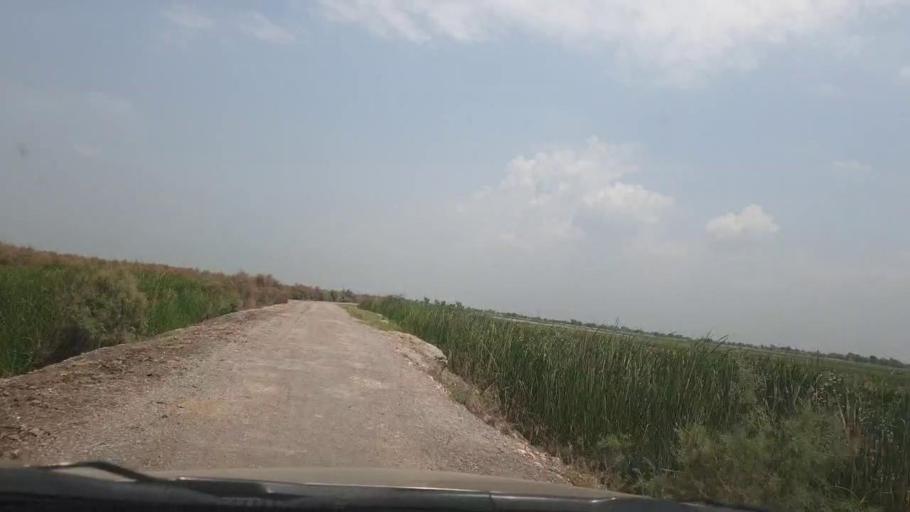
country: PK
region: Sindh
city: Naudero
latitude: 27.7223
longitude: 68.3212
